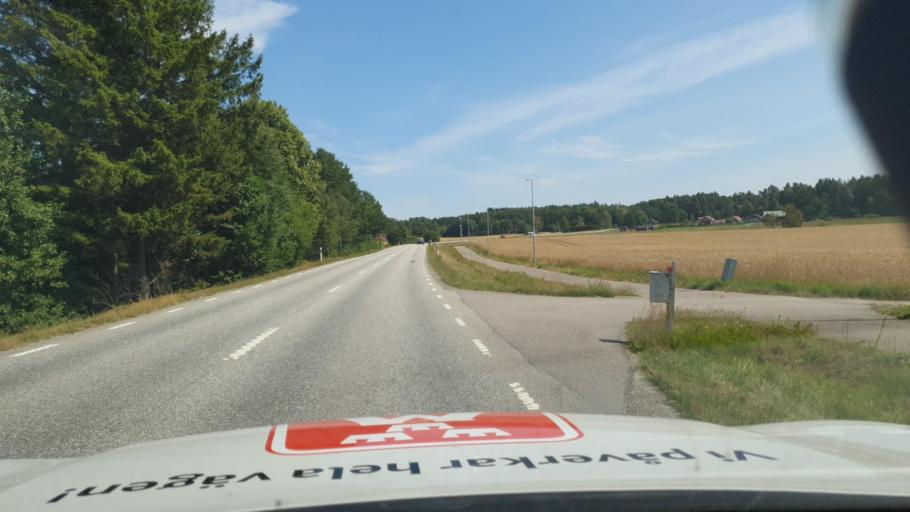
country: SE
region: Vaestra Goetaland
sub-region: Alingsas Kommun
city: Sollebrunn
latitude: 58.1179
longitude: 12.5489
